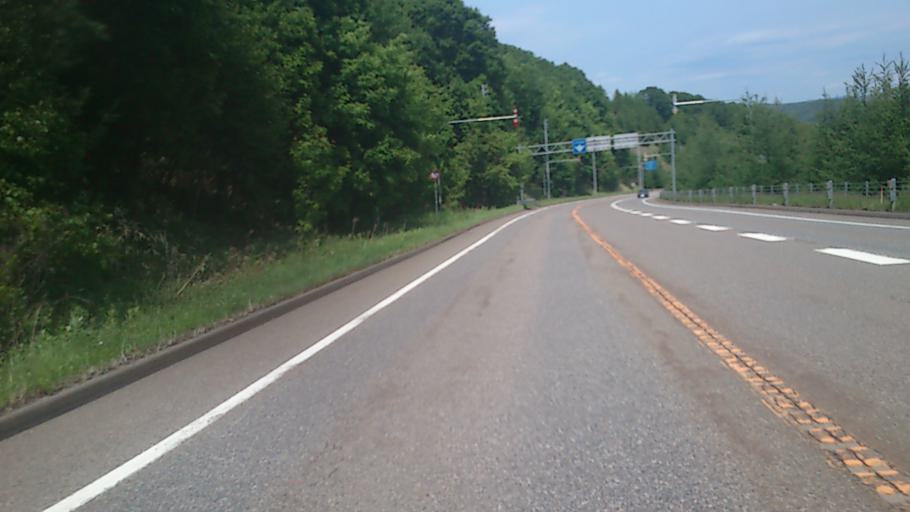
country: JP
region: Hokkaido
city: Otofuke
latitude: 43.2359
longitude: 143.5290
